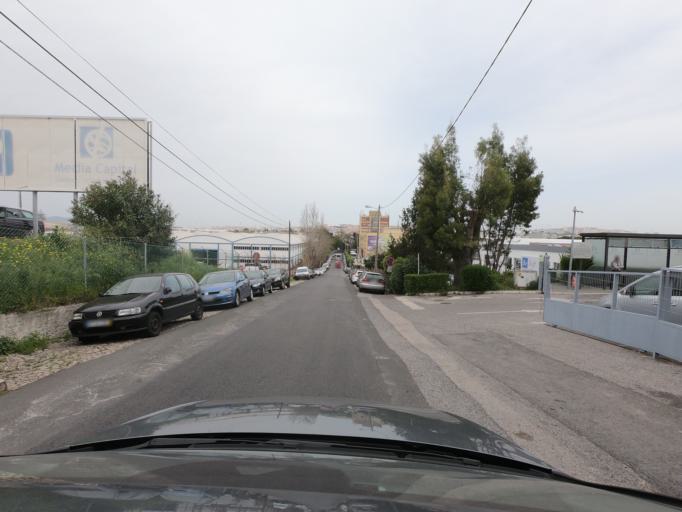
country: PT
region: Lisbon
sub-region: Oeiras
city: Barcarena
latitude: 38.7398
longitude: -9.2681
